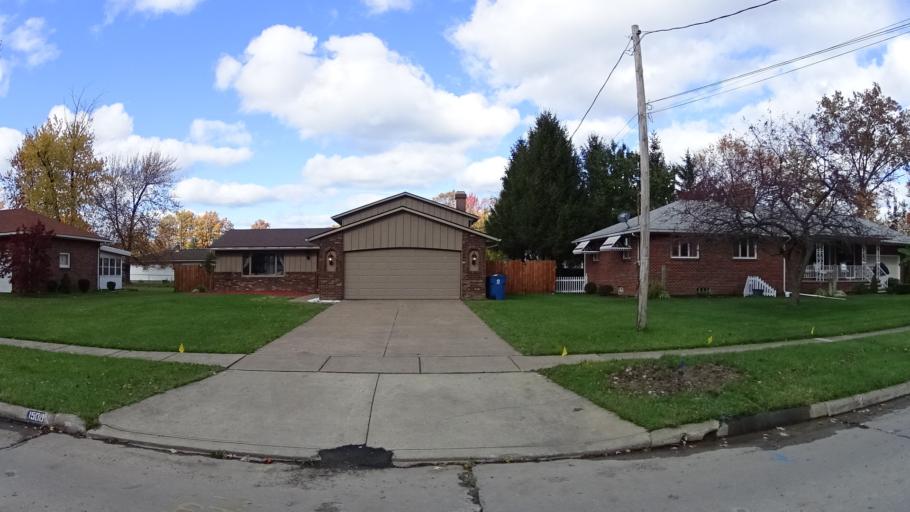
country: US
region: Ohio
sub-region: Lorain County
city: Lorain
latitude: 41.4344
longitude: -82.1913
